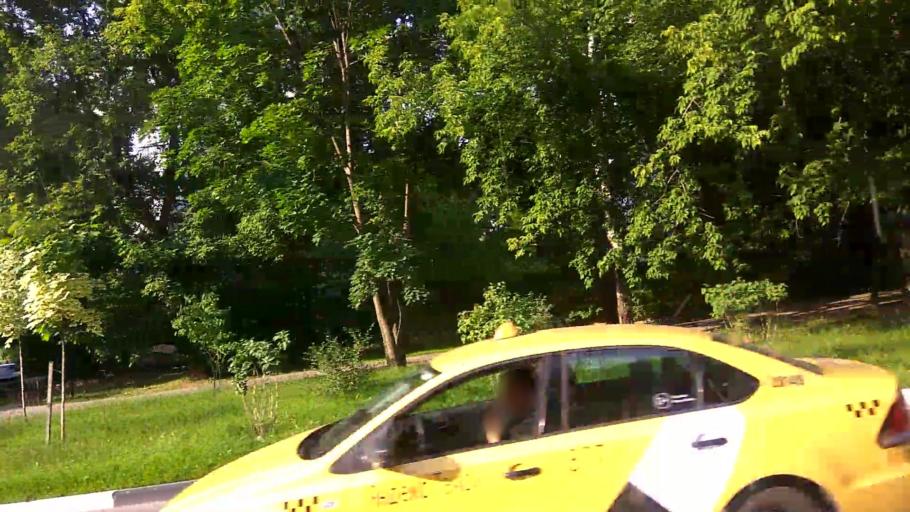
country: RU
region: Moskovskaya
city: Mytishchi
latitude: 55.9053
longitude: 37.7096
